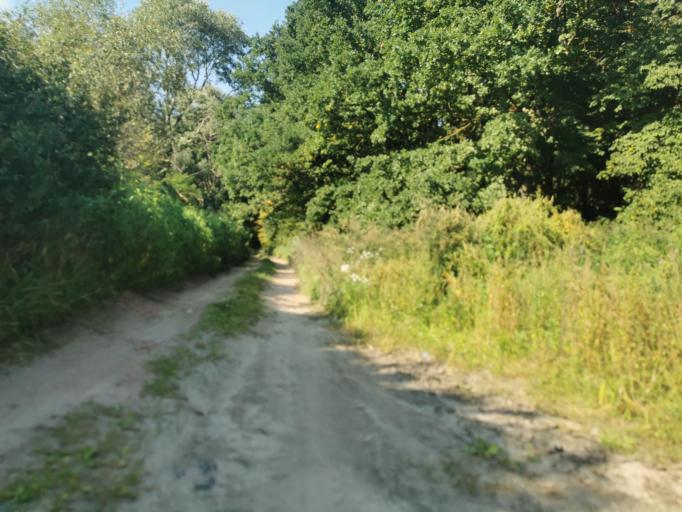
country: SK
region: Trnavsky
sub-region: Okres Senica
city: Senica
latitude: 48.6257
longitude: 17.2315
